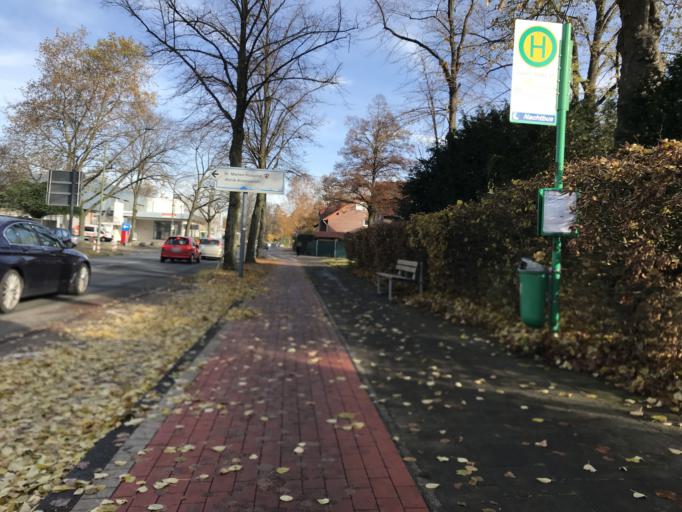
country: DE
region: North Rhine-Westphalia
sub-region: Regierungsbezirk Arnsberg
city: Hamm
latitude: 51.6866
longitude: 7.8488
